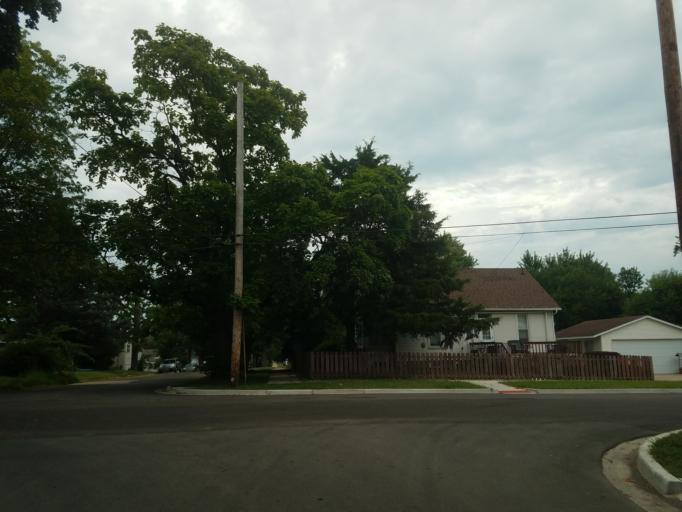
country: US
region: Illinois
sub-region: McLean County
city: Bloomington
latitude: 40.4859
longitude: -88.9817
